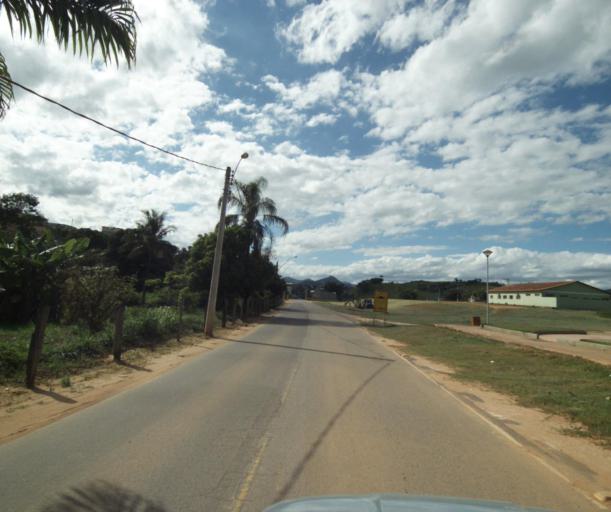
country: BR
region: Espirito Santo
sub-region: Sao Jose Do Calcado
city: Sao Jose do Calcado
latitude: -21.0425
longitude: -41.6520
